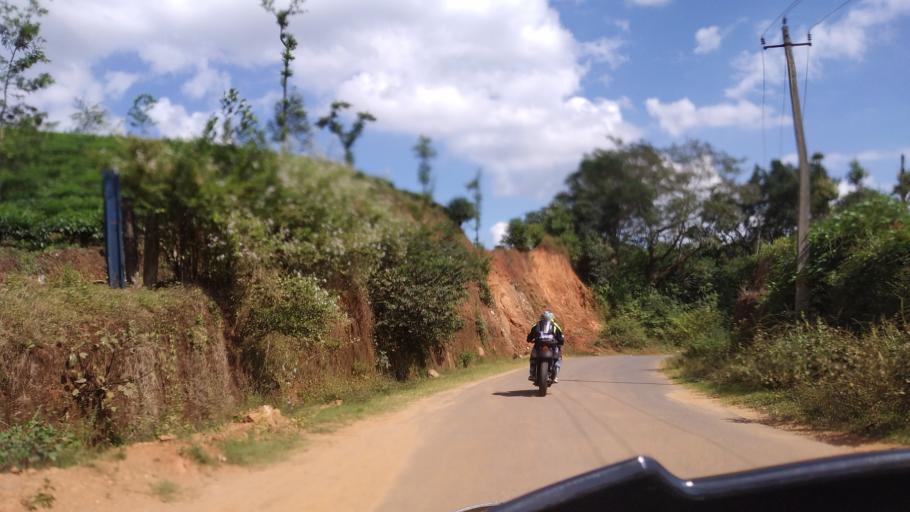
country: IN
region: Karnataka
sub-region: Kodagu
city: Ponnampet
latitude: 12.0330
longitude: 75.9341
